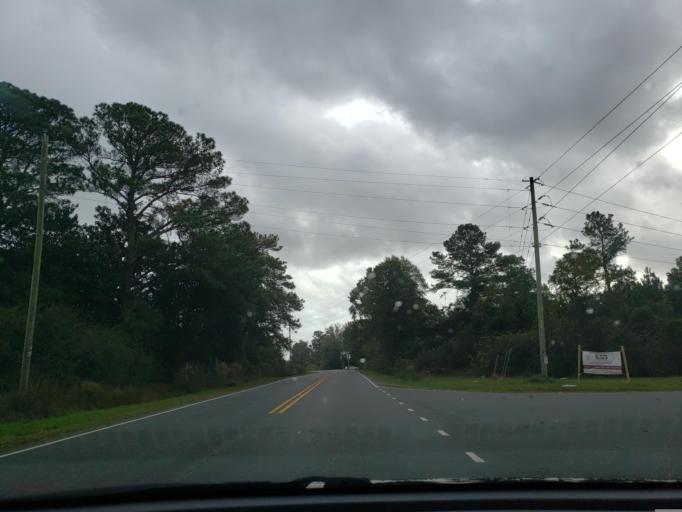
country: US
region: North Carolina
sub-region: Duplin County
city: Beulaville
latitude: 34.8486
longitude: -77.8705
